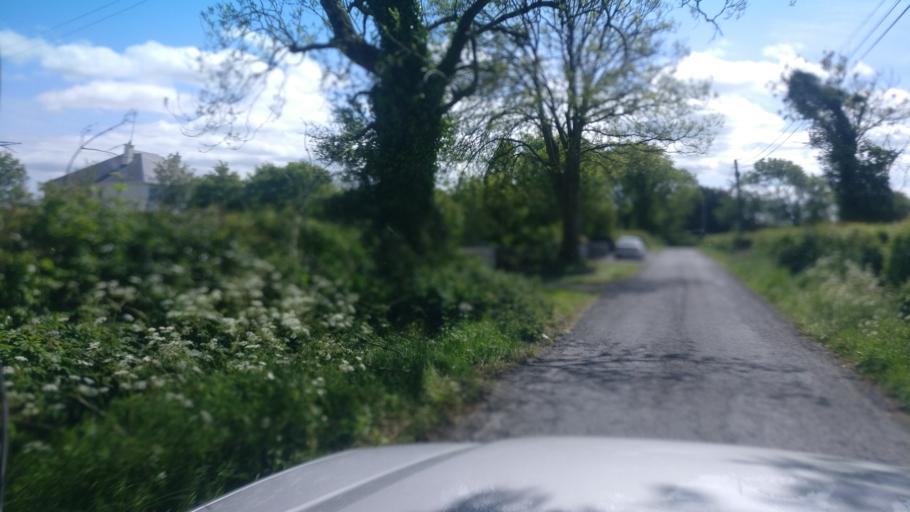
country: IE
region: Connaught
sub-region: County Galway
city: Gort
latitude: 53.1483
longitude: -8.7438
